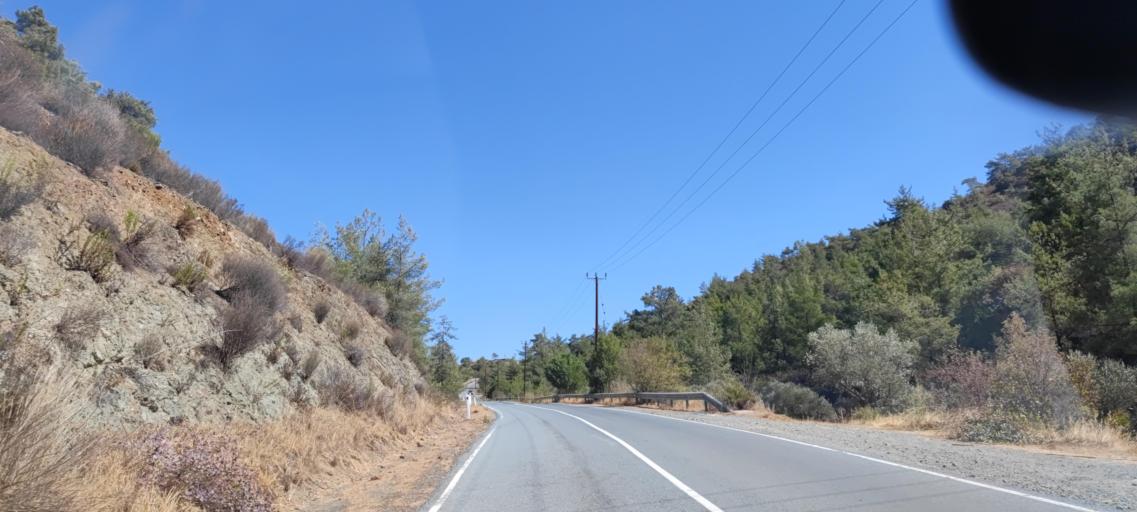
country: CY
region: Limassol
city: Pelendri
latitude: 34.8266
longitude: 33.0212
